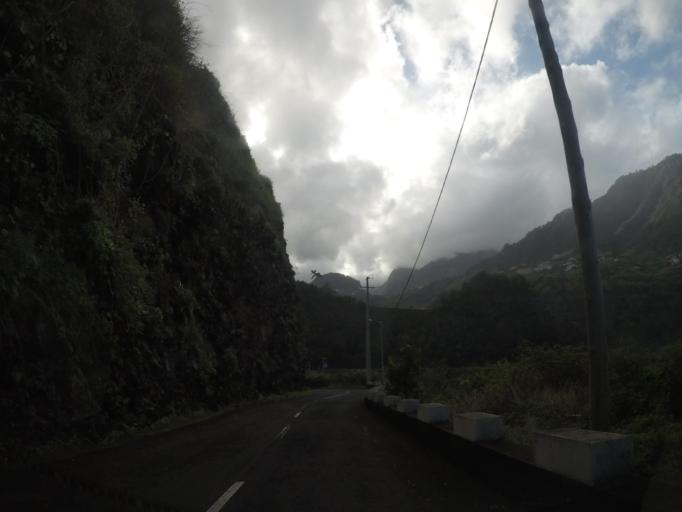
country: PT
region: Madeira
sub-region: Santana
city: Santana
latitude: 32.7862
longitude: -16.8486
